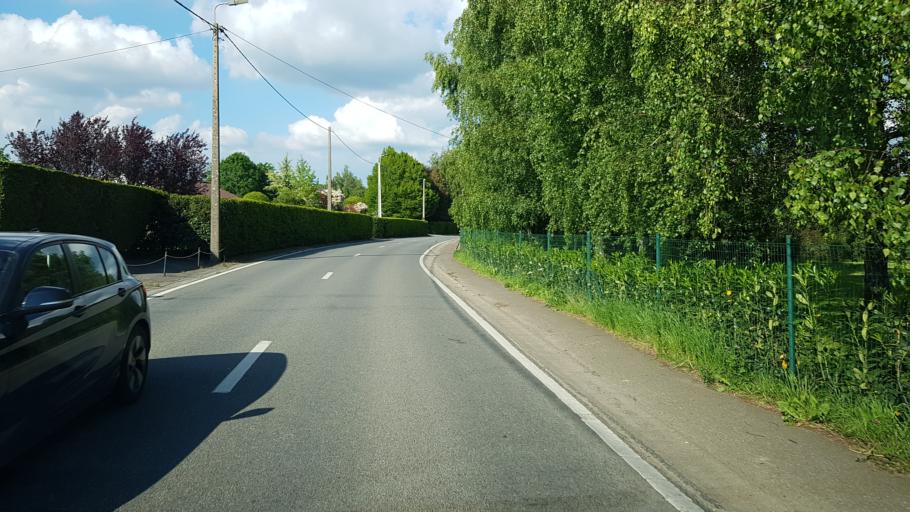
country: BE
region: Wallonia
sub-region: Province de Liege
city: Sprimont
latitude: 50.5378
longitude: 5.6379
